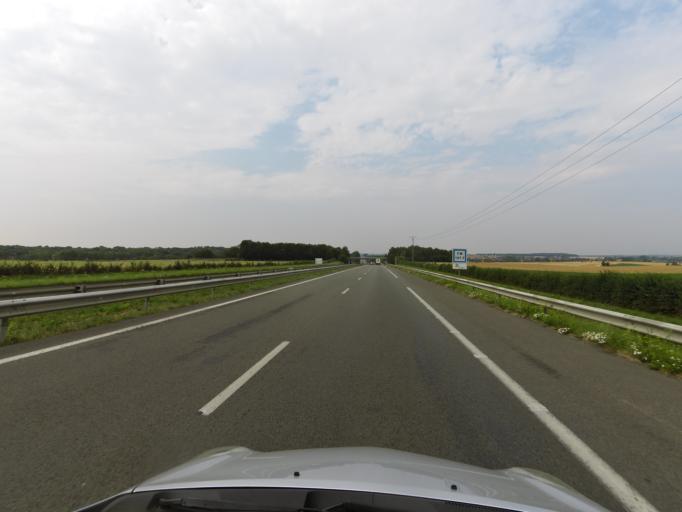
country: FR
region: Nord-Pas-de-Calais
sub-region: Departement du Nord
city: Marcoing
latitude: 50.1035
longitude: 3.1656
